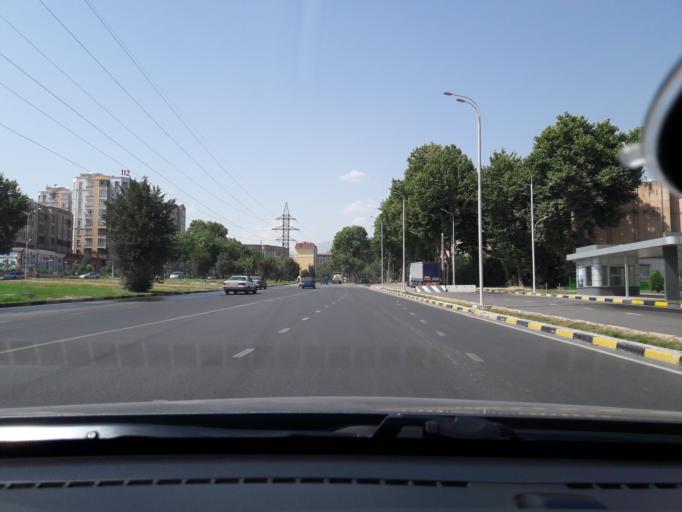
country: TJ
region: Dushanbe
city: Dushanbe
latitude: 38.5864
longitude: 68.7413
